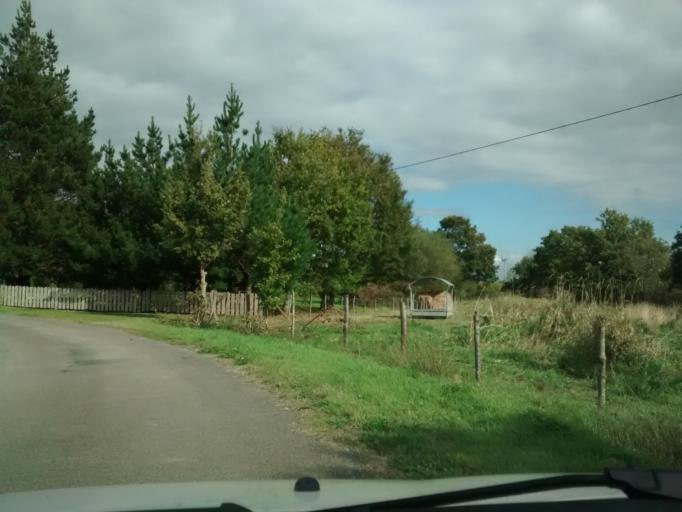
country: FR
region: Pays de la Loire
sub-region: Departement de la Loire-Atlantique
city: Saint-Viaud
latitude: 47.2763
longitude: -1.9957
